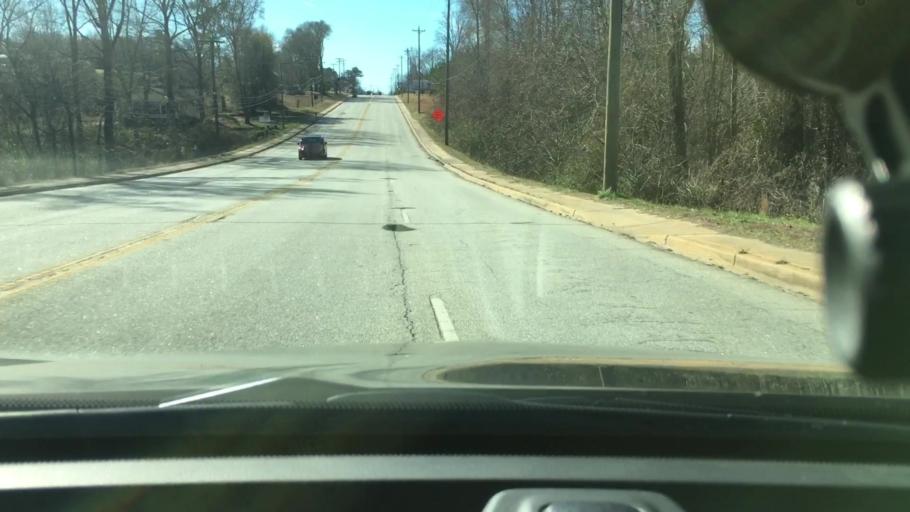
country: US
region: South Carolina
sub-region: Cherokee County
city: East Gaffney
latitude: 35.0996
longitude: -81.6281
